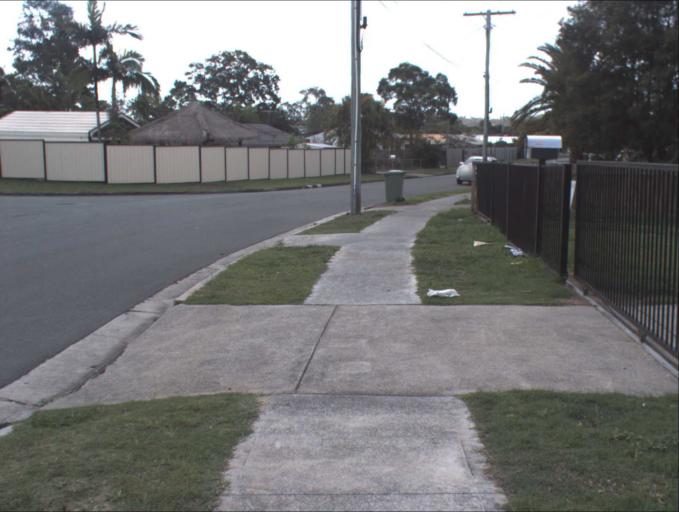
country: AU
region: Queensland
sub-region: Logan
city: Waterford West
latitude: -27.6928
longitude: 153.1537
